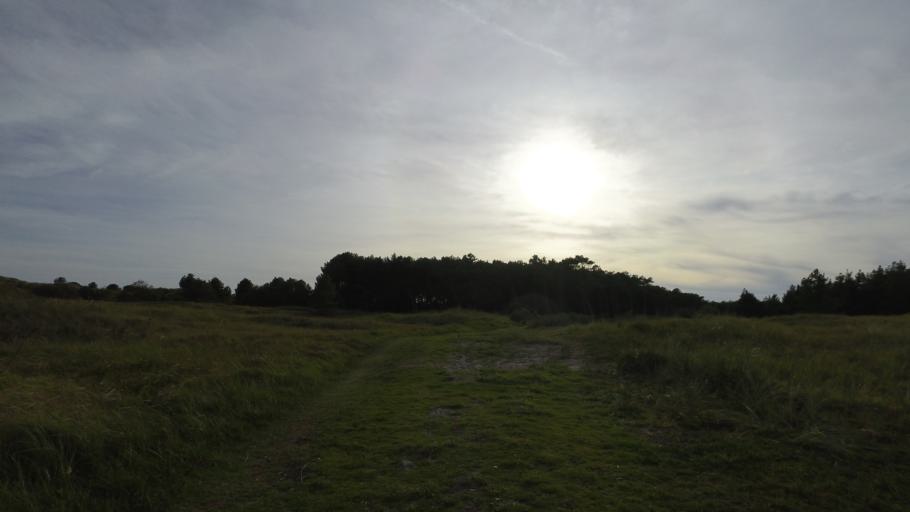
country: NL
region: Friesland
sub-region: Gemeente Ameland
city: Nes
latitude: 53.4592
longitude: 5.8226
